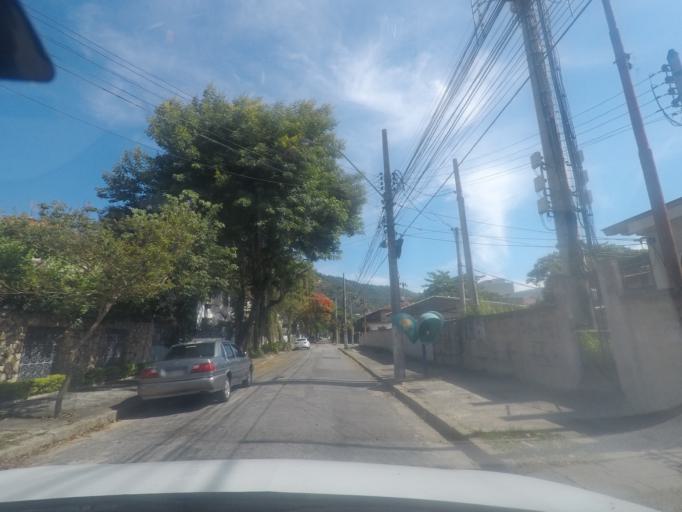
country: BR
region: Rio de Janeiro
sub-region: Niteroi
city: Niteroi
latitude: -22.9183
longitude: -43.0922
